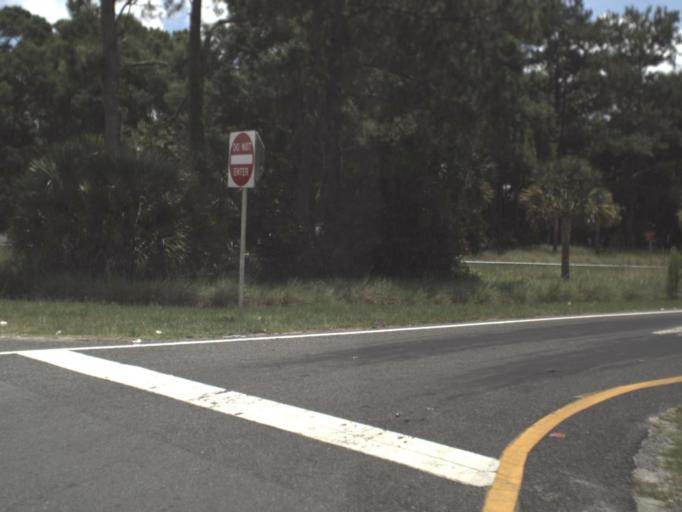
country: US
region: Florida
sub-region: Suwannee County
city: Wellborn
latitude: 30.3161
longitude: -82.8087
